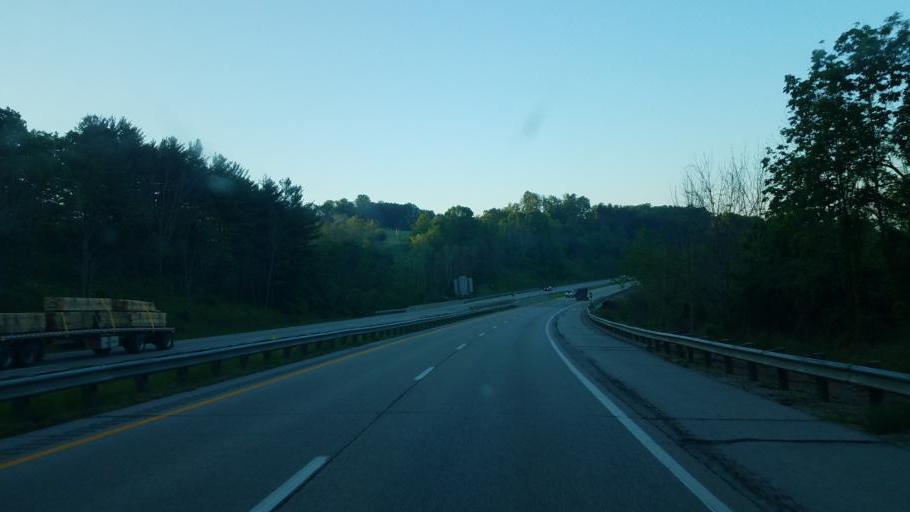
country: US
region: Ohio
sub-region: Washington County
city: Devola
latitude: 39.4697
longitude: -81.4361
